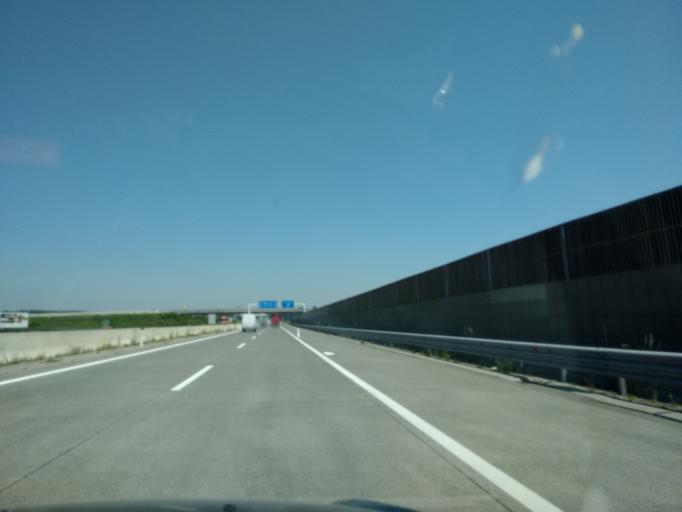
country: AT
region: Upper Austria
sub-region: Politischer Bezirk Gmunden
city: Vorchdorf
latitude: 48.0091
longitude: 13.9204
